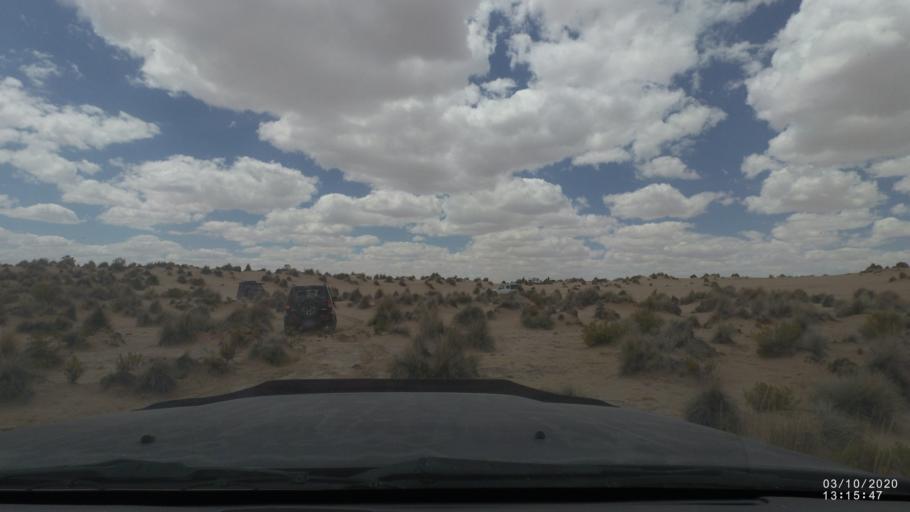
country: BO
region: Oruro
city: Poopo
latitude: -18.6912
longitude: -67.5336
